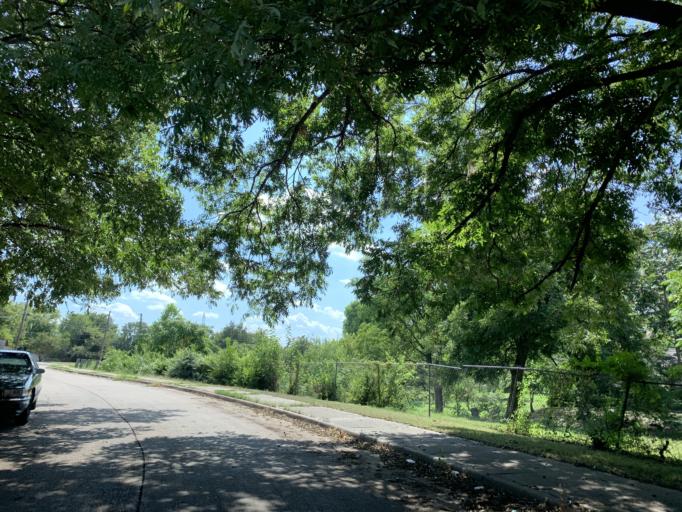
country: US
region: Texas
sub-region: Dallas County
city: Hutchins
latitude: 32.7087
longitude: -96.7654
